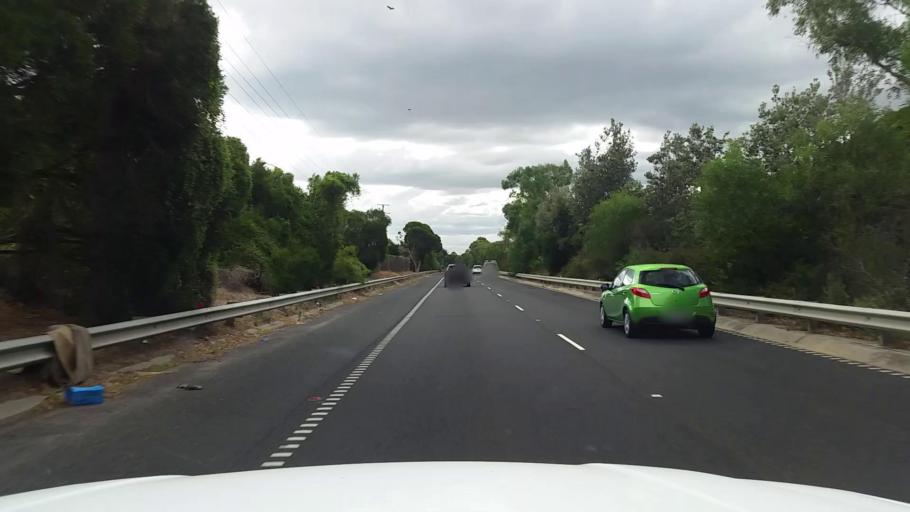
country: AU
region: Victoria
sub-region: Frankston
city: Frankston East
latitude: -38.1384
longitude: 145.1366
